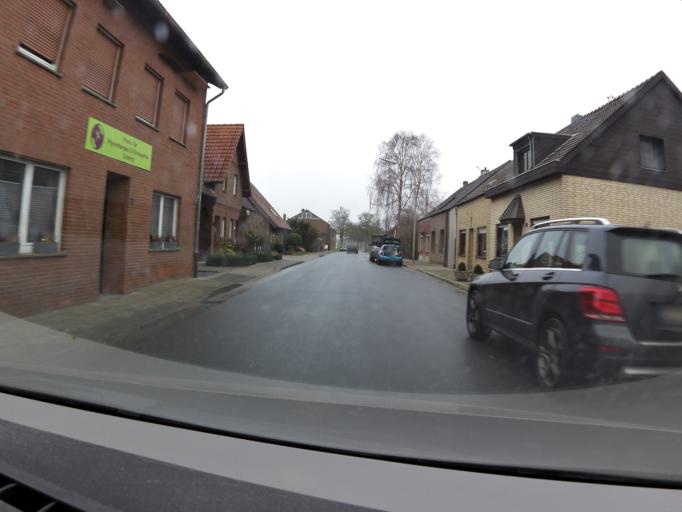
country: DE
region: North Rhine-Westphalia
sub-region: Regierungsbezirk Dusseldorf
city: Sonsbeck
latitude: 51.5736
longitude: 6.3576
